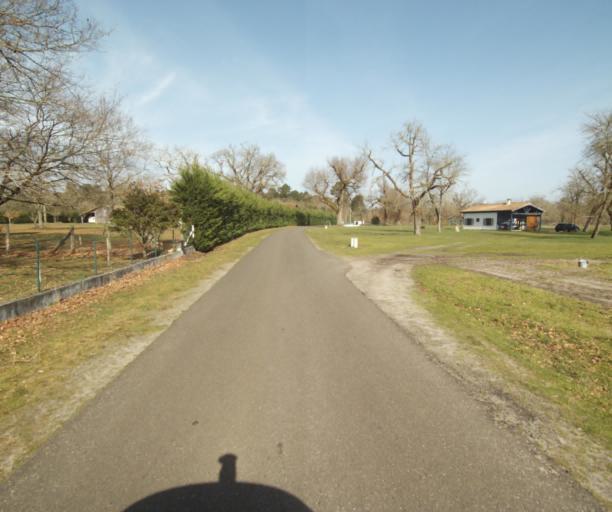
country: FR
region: Aquitaine
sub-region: Departement des Landes
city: Roquefort
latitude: 44.1317
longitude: -0.2500
